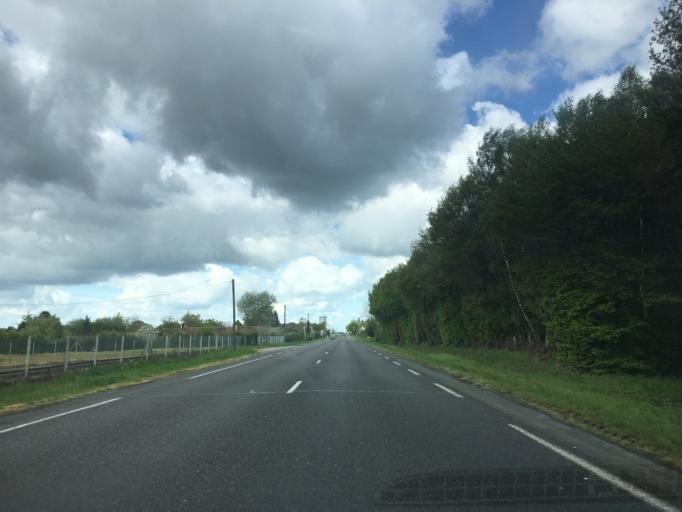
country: FR
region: Lower Normandy
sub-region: Departement de l'Orne
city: Saint-Sulpice-sur-Risle
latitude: 48.7571
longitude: 0.6996
